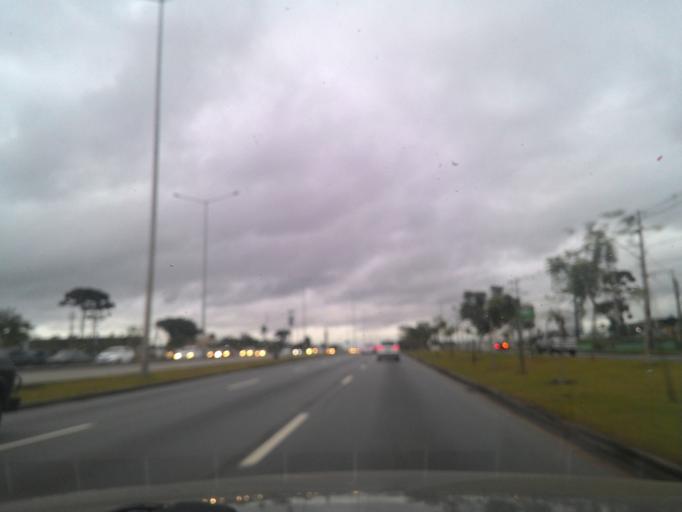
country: BR
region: Parana
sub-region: Curitiba
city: Curitiba
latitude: -25.4925
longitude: -49.2725
